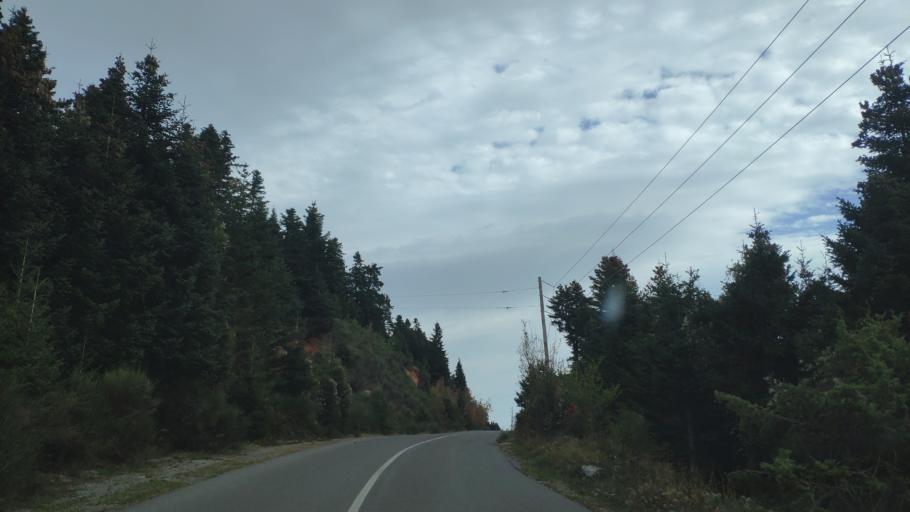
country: GR
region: Central Greece
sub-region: Nomos Fokidos
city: Amfissa
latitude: 38.7029
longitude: 22.3194
